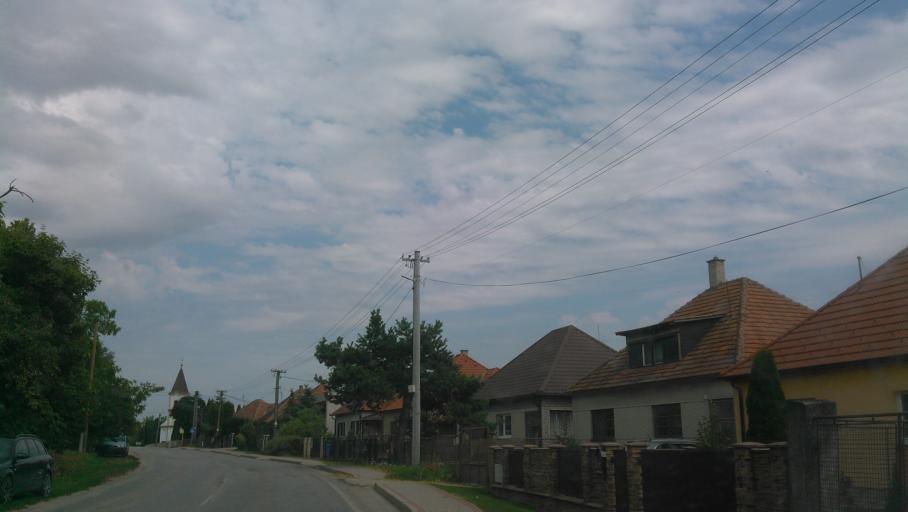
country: SK
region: Trnavsky
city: Hlohovec
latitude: 48.4425
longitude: 17.9009
